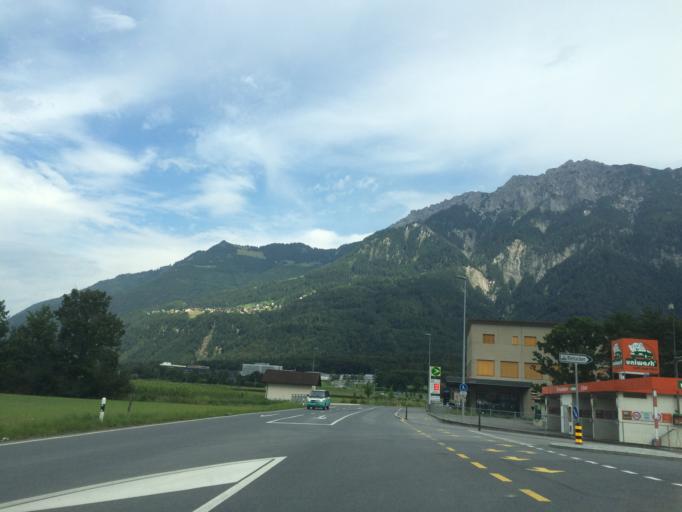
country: LI
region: Schaan
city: Schaan
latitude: 47.1780
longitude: 9.5102
